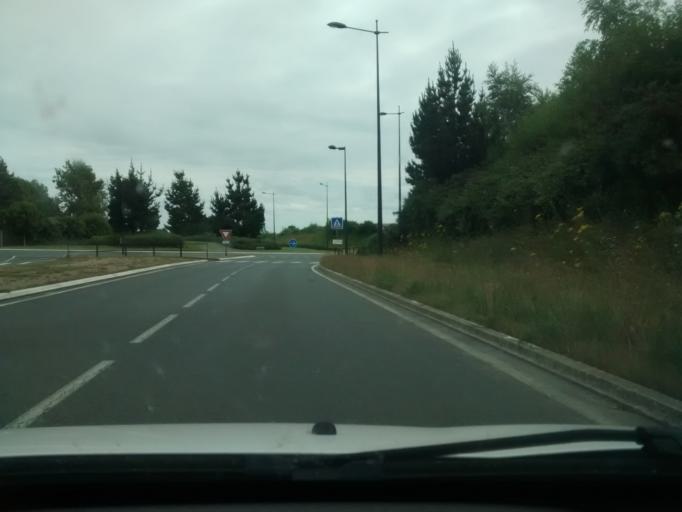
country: FR
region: Brittany
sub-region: Departement des Cotes-d'Armor
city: Lannion
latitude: 48.7521
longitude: -3.4491
